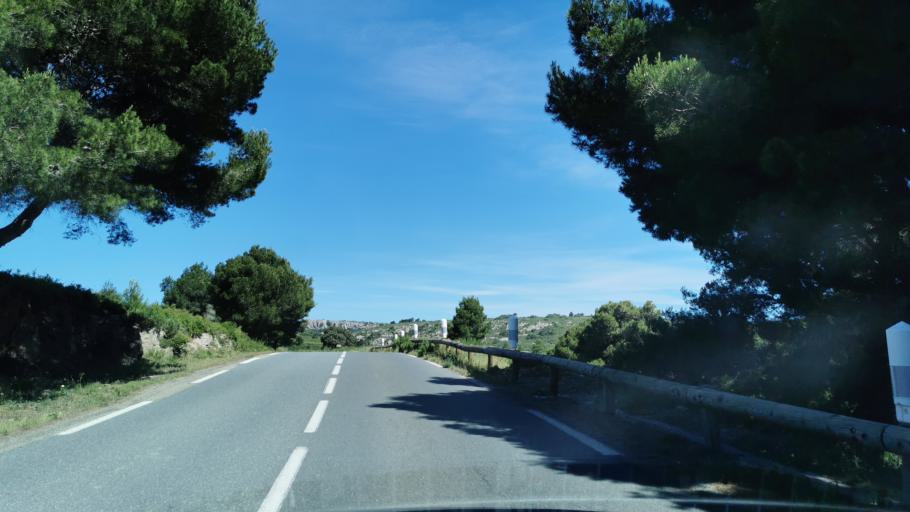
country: FR
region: Languedoc-Roussillon
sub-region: Departement de l'Aude
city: Armissan
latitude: 43.1574
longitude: 3.1519
